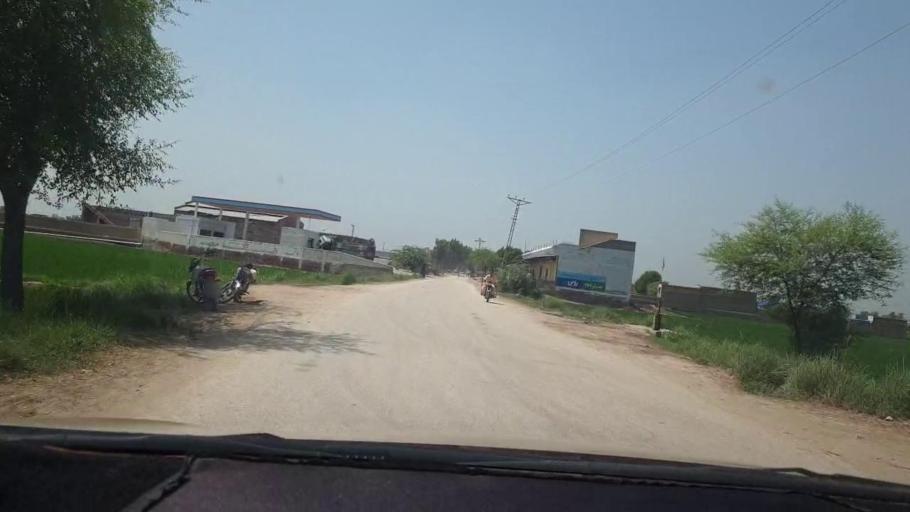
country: PK
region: Sindh
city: Kambar
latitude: 27.5954
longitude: 68.0189
